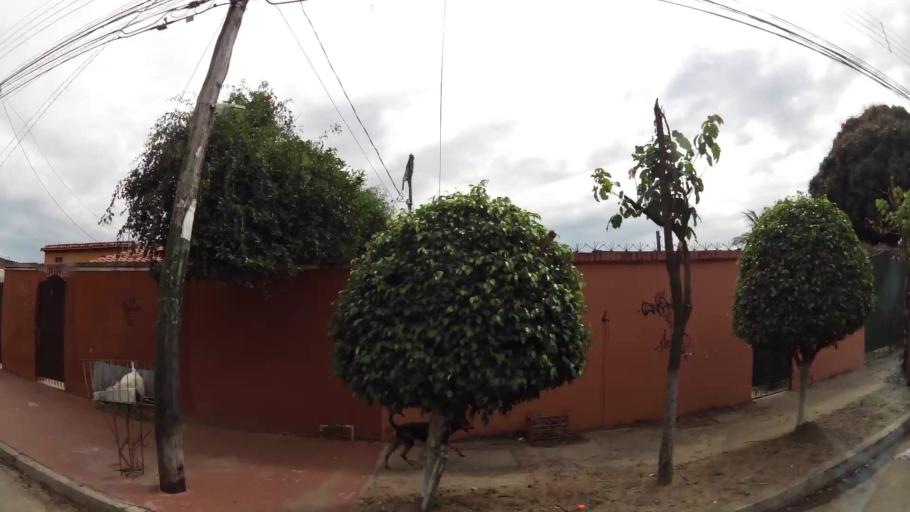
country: BO
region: Santa Cruz
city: Santa Cruz de la Sierra
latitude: -17.7467
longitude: -63.1920
